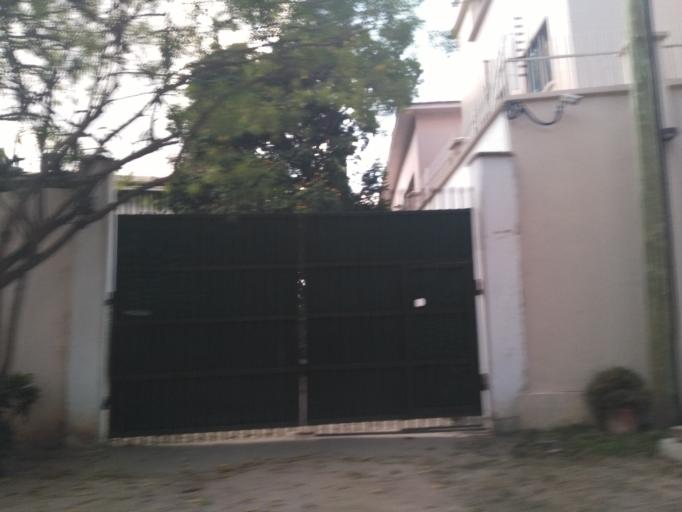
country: TZ
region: Dar es Salaam
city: Magomeni
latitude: -6.7760
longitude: 39.2564
